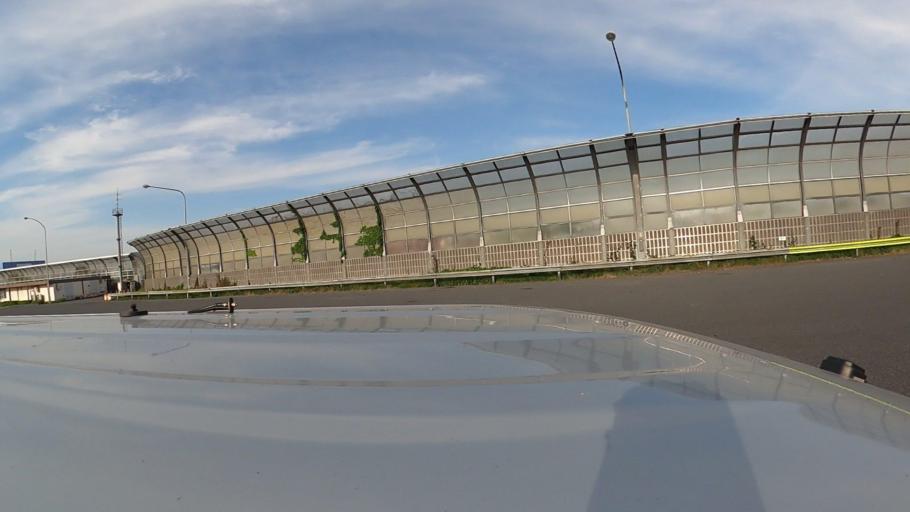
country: JP
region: Saitama
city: Asaka
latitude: 35.7735
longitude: 139.5689
